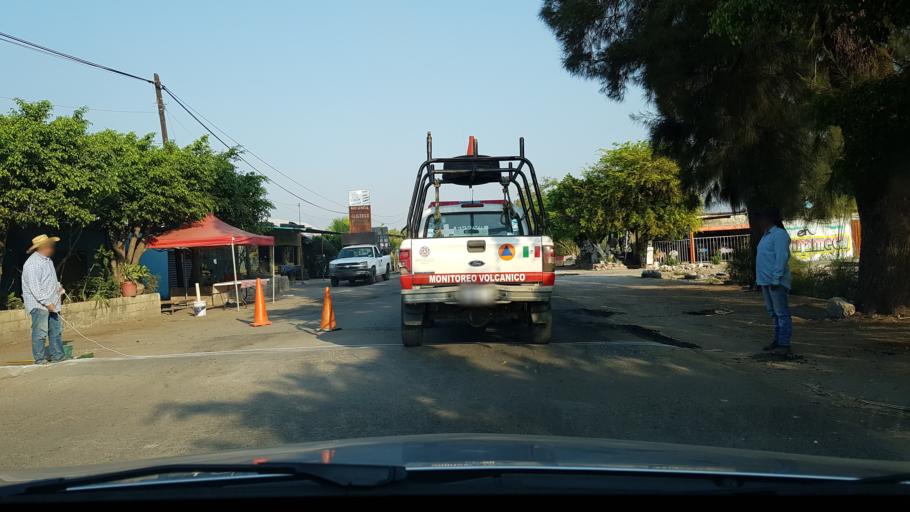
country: MX
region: Morelos
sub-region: Tepalcingo
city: Zacapalco
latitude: 18.6263
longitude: -99.0038
